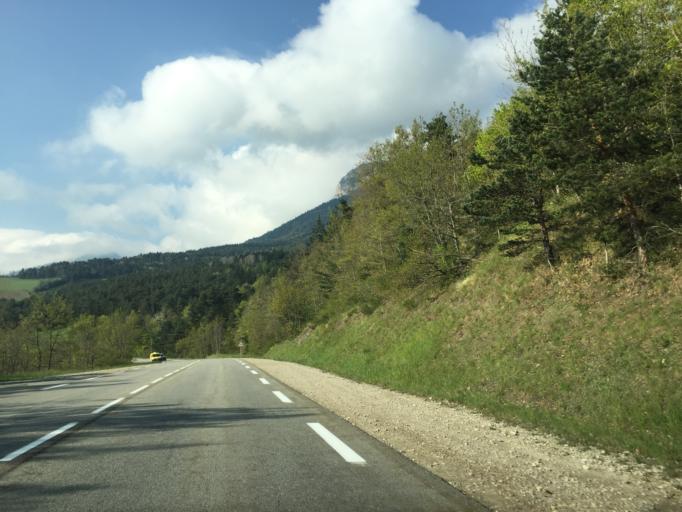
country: FR
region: Rhone-Alpes
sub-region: Departement de l'Isere
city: Mens
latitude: 44.8096
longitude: 5.6294
